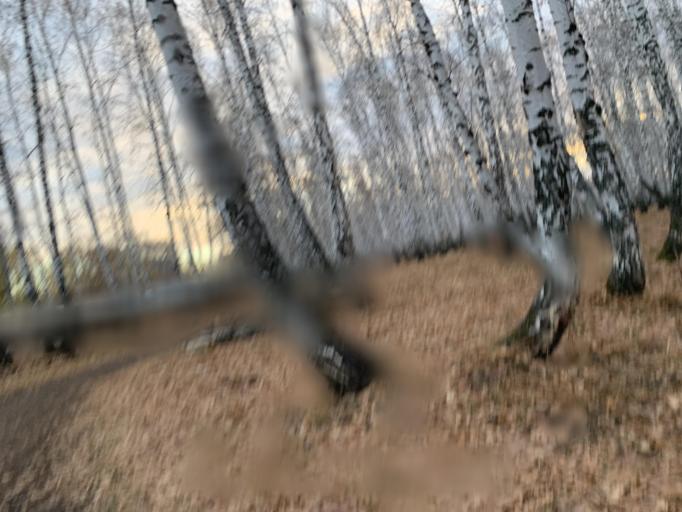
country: RU
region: Chelyabinsk
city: Roshchino
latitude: 55.2034
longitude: 61.3128
